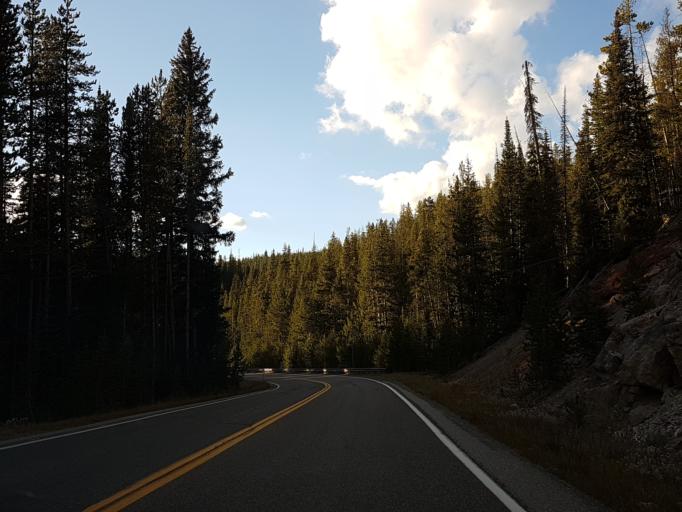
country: US
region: Montana
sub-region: Gallatin County
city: West Yellowstone
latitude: 44.4374
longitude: -110.7284
